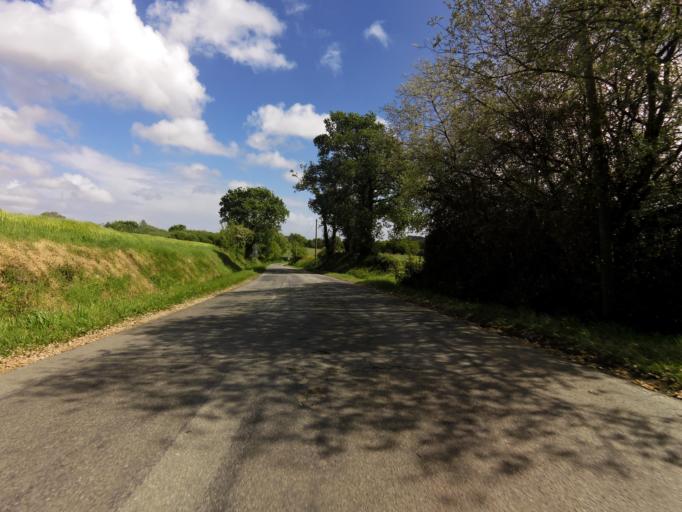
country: FR
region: Brittany
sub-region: Departement du Morbihan
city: Plougoumelen
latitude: 47.6551
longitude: -2.9030
